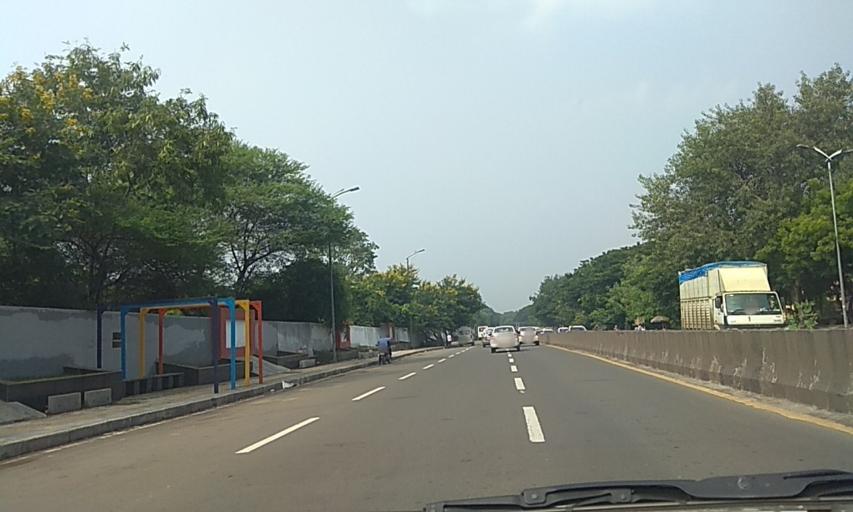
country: IN
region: Maharashtra
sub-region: Pune Division
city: Khadki
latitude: 18.5526
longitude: 73.8779
